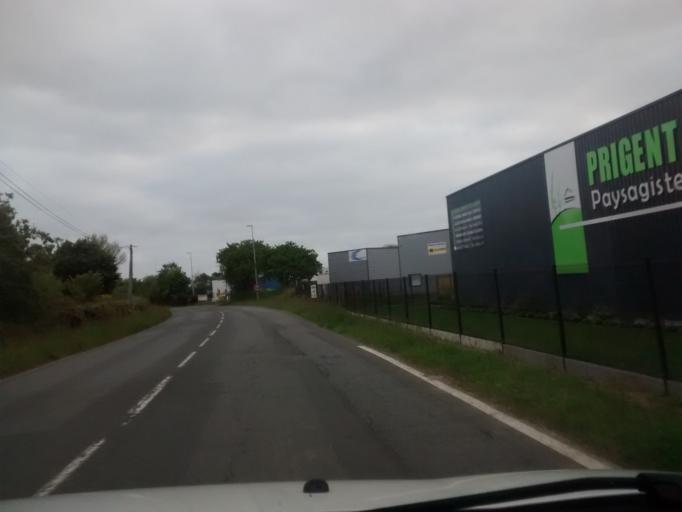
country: FR
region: Brittany
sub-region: Departement des Cotes-d'Armor
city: Tregastel
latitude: 48.8027
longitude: -3.4740
